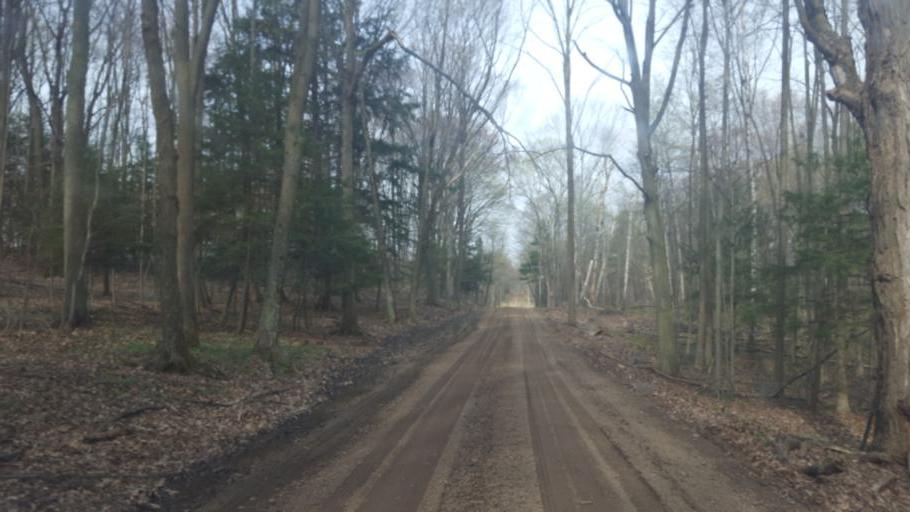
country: US
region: Michigan
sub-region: Isabella County
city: Lake Isabella
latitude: 43.5177
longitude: -84.9397
